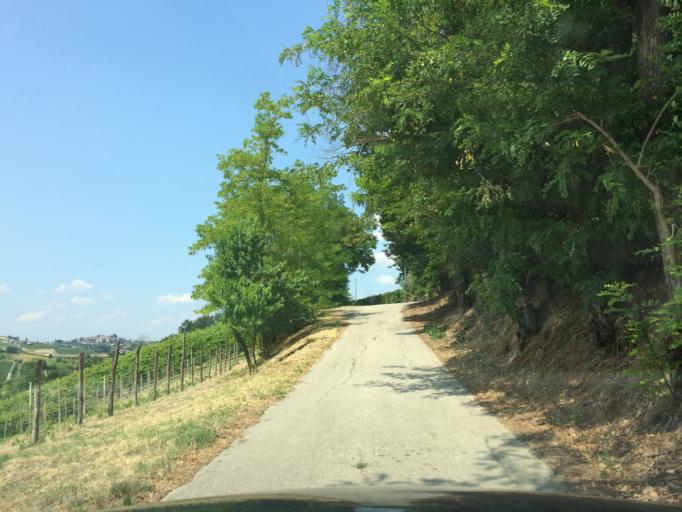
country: IT
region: Piedmont
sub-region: Provincia di Asti
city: Moasca
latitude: 44.7609
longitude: 8.2604
